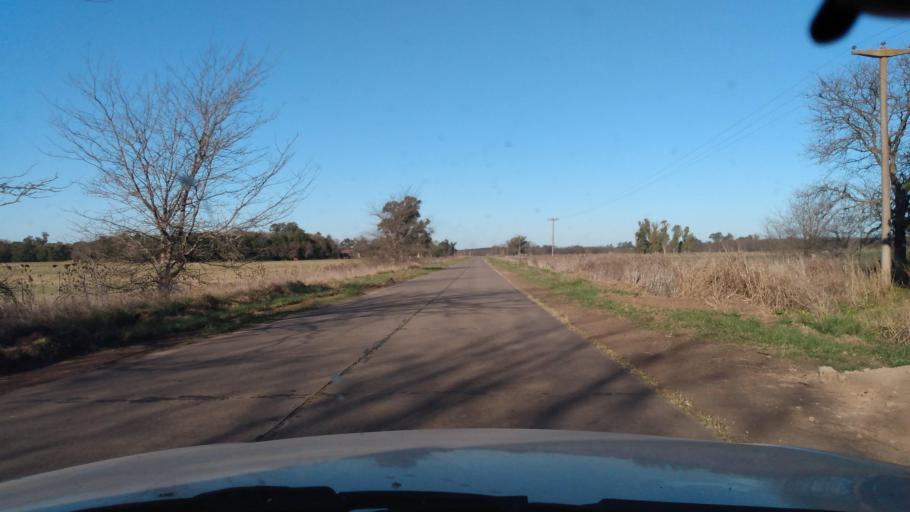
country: AR
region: Buenos Aires
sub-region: Partido de Mercedes
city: Mercedes
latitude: -34.6138
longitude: -59.2743
